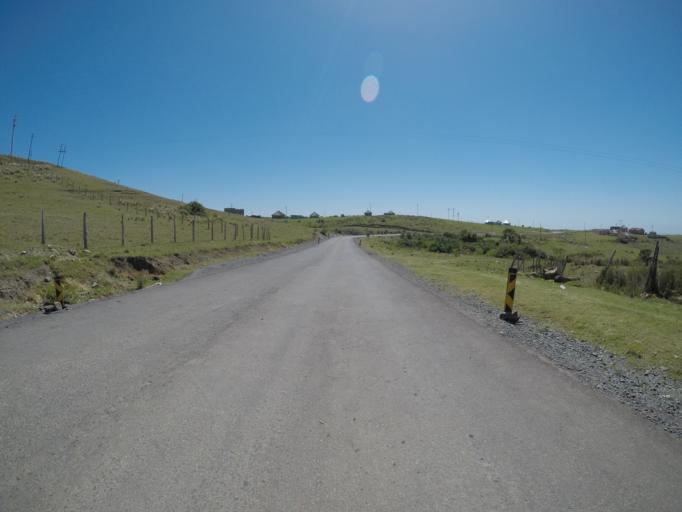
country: ZA
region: Eastern Cape
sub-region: OR Tambo District Municipality
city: Libode
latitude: -31.9999
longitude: 29.1199
